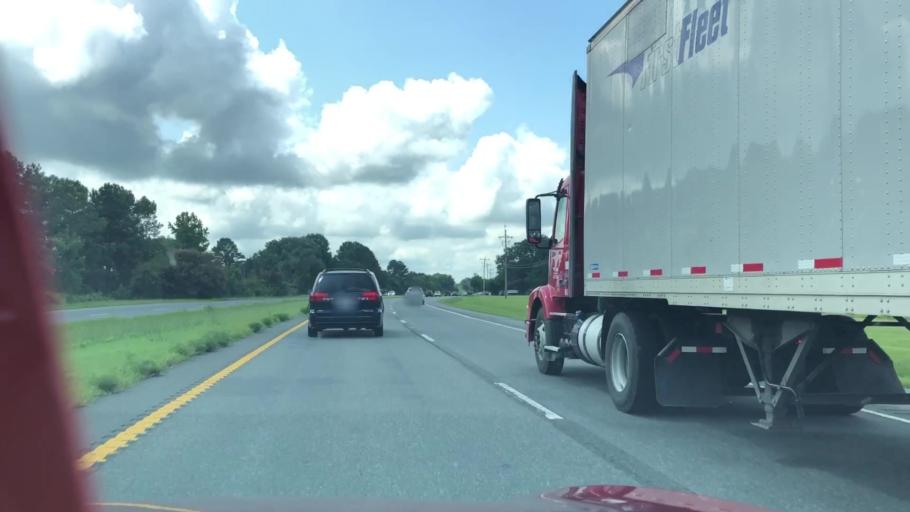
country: US
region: Virginia
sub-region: Accomack County
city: Onancock
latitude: 37.6794
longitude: -75.7234
